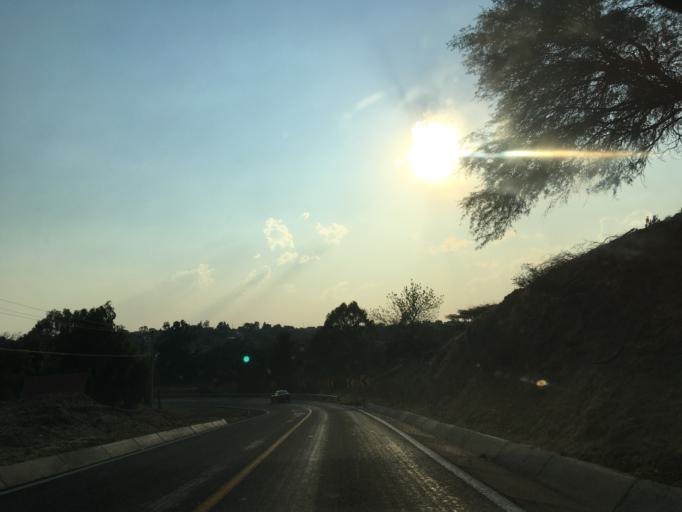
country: MX
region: Michoacan
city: Charo
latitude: 19.7551
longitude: -101.0421
